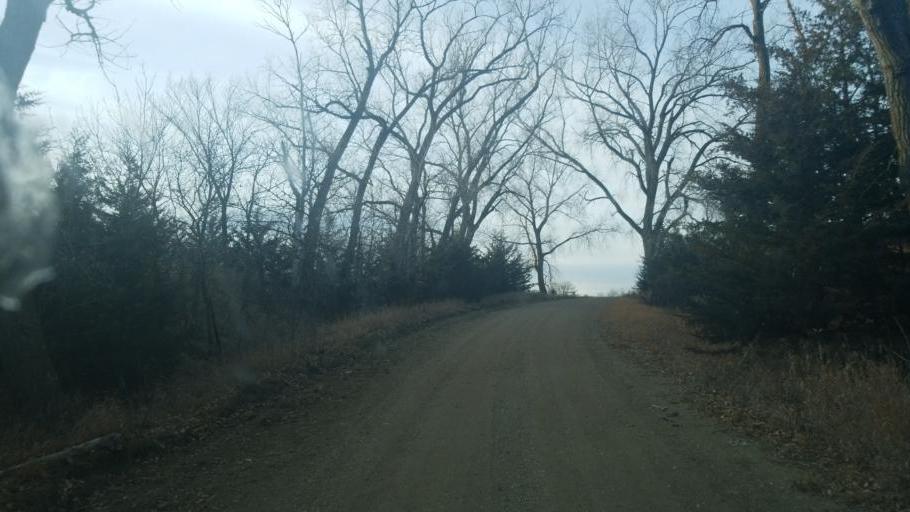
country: US
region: Nebraska
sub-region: Knox County
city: Center
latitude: 42.6811
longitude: -97.8177
